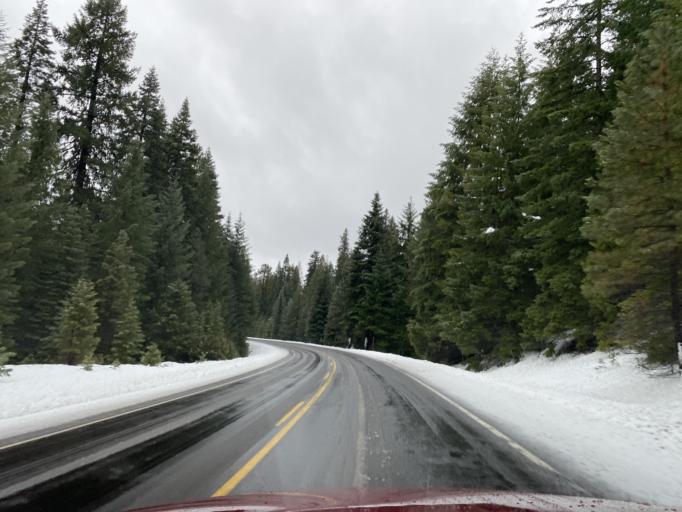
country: US
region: Oregon
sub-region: Klamath County
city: Klamath Falls
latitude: 42.4956
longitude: -122.0852
